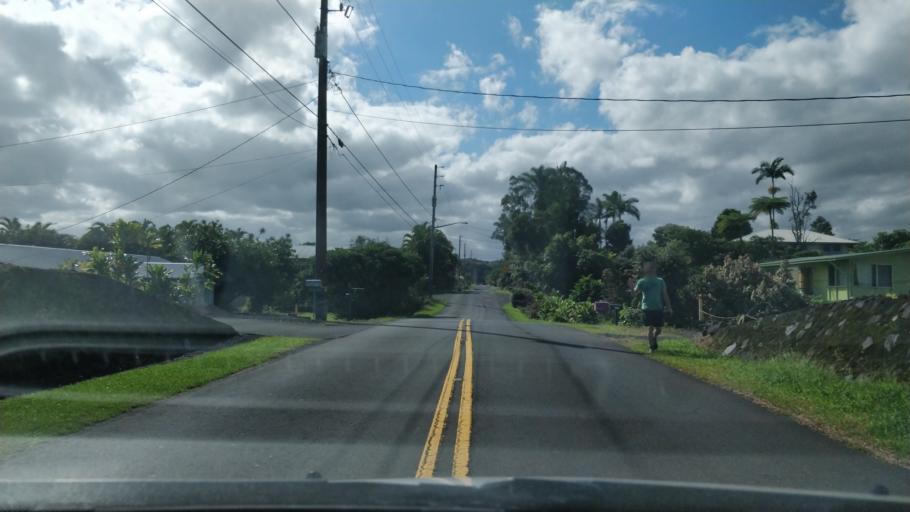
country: US
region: Hawaii
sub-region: Hawaii County
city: Hilo
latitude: 19.6712
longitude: -155.1057
